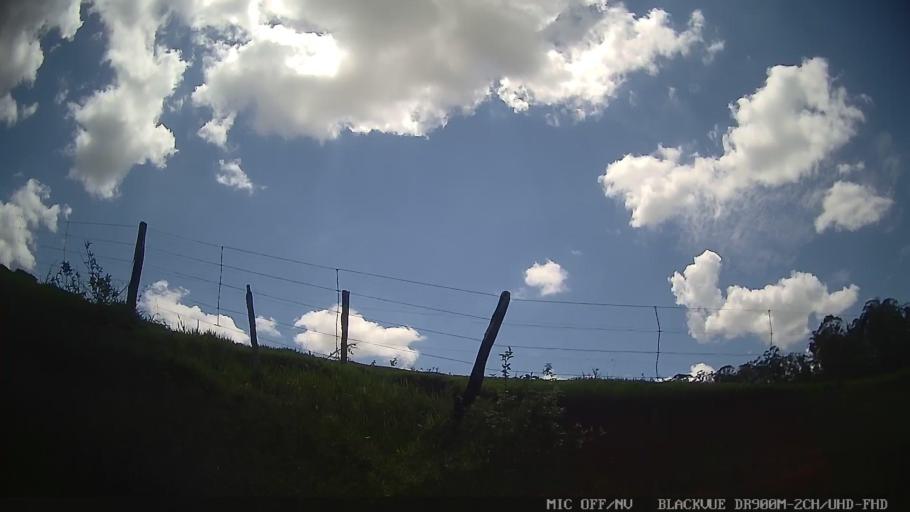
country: BR
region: Sao Paulo
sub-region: Itatiba
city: Itatiba
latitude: -22.8687
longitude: -46.7877
